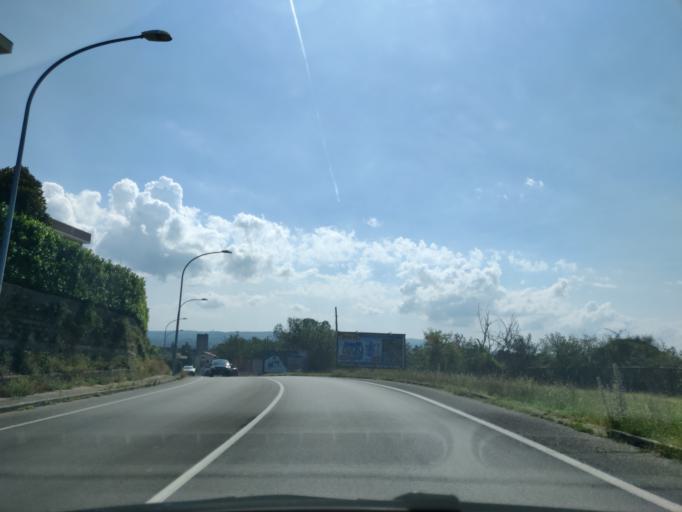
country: IT
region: Latium
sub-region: Provincia di Viterbo
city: Viterbo
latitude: 42.4209
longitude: 12.0946
